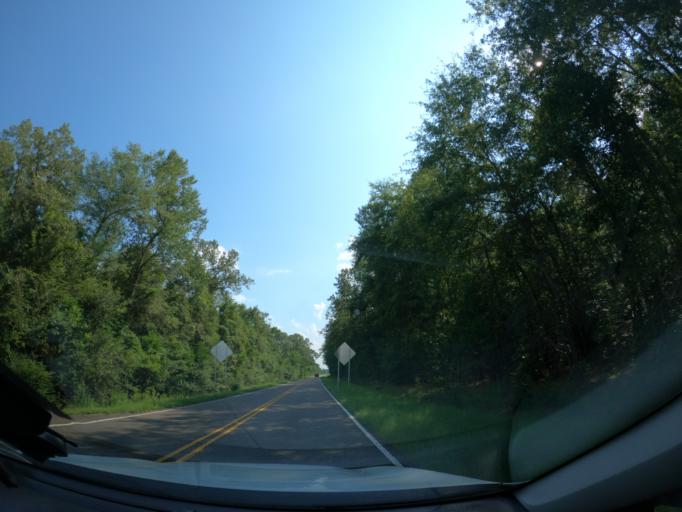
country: US
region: South Carolina
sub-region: Barnwell County
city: Williston
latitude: 33.5748
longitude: -81.4778
